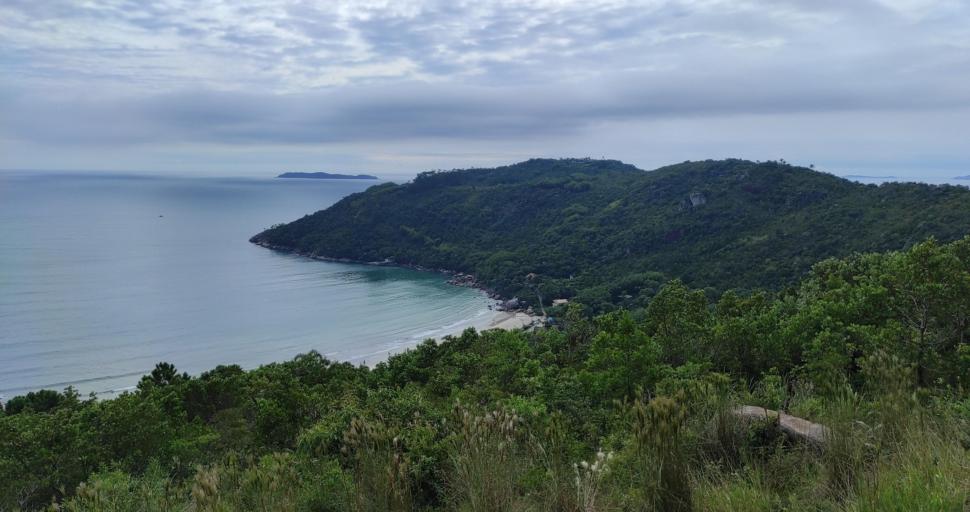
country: BR
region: Santa Catarina
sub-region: Porto Belo
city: Porto Belo
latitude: -27.2028
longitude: -48.4958
